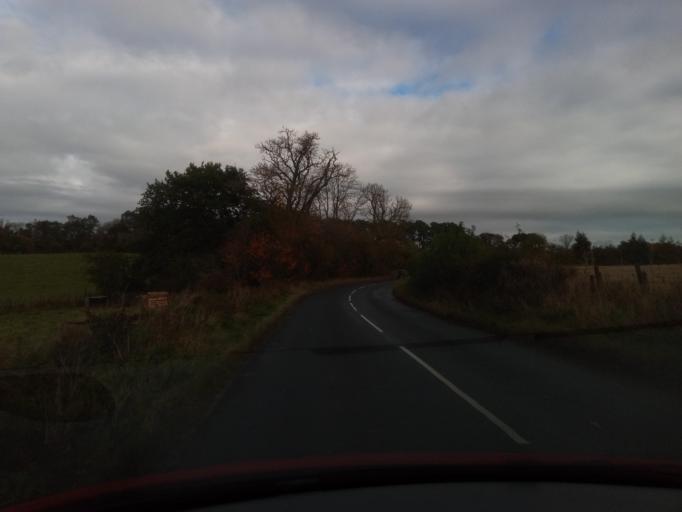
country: GB
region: Scotland
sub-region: The Scottish Borders
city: Newtown St Boswells
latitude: 55.5607
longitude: -2.7085
